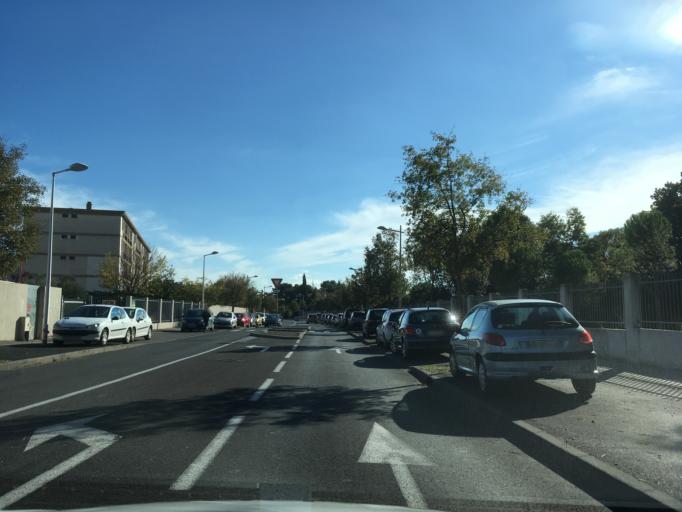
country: FR
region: Languedoc-Roussillon
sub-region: Departement de l'Herault
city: Montpellier
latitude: 43.6104
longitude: 3.8465
